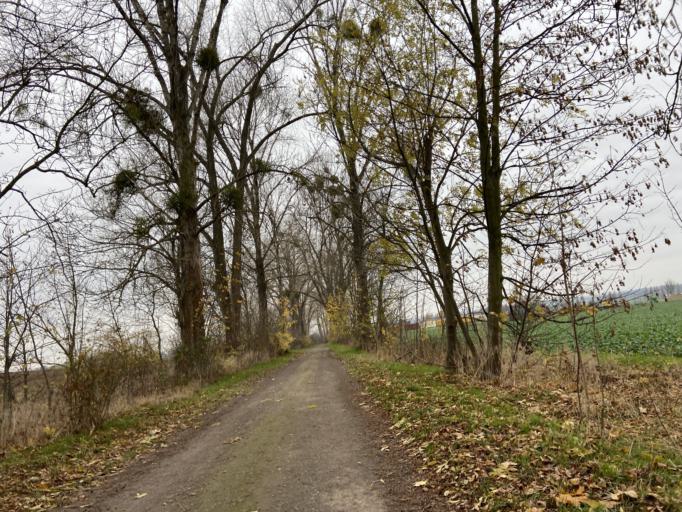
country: DE
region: Lower Saxony
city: Erkerode
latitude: 52.2179
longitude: 10.7030
